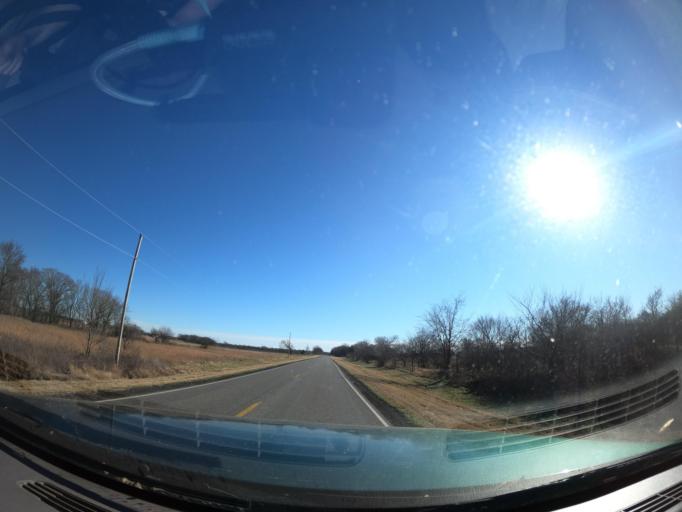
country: US
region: Oklahoma
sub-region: McIntosh County
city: Checotah
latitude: 35.5696
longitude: -95.6564
